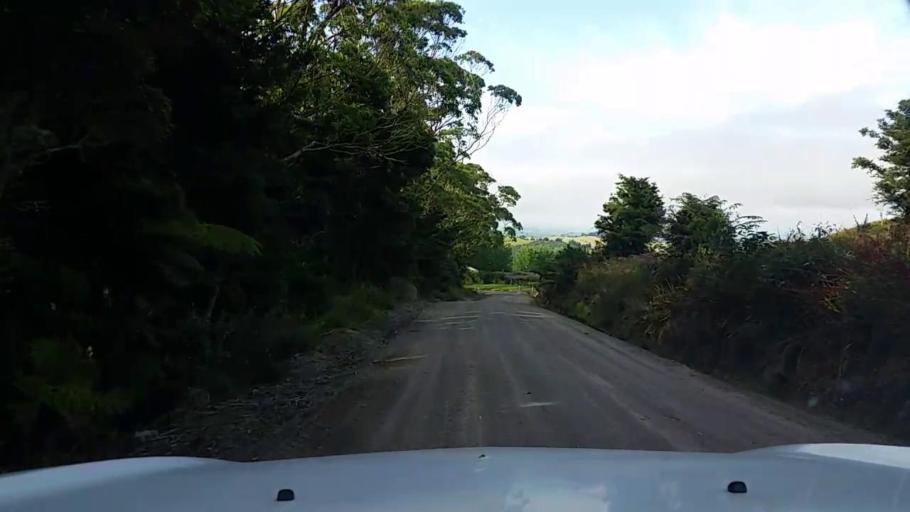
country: NZ
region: Northland
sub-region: Whangarei
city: Maungatapere
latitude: -35.6695
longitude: 174.1757
